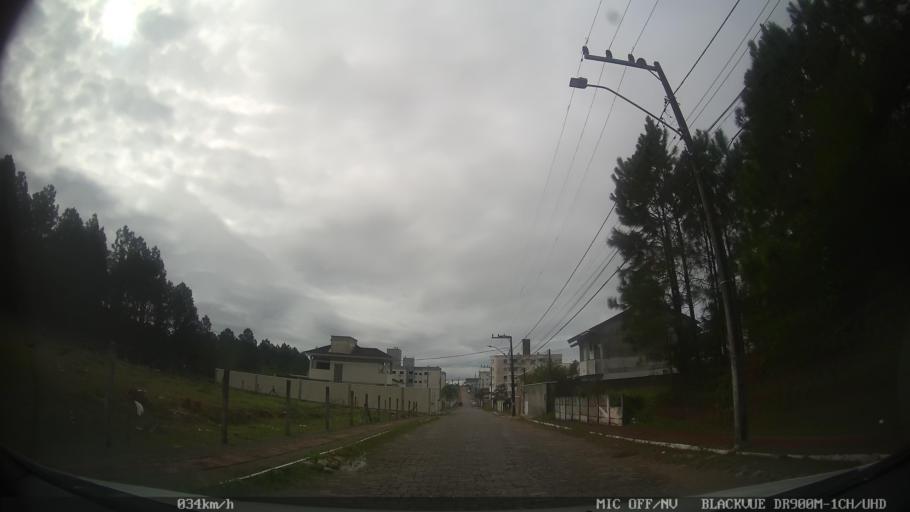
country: BR
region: Santa Catarina
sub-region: Sao Jose
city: Campinas
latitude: -27.5526
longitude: -48.6370
